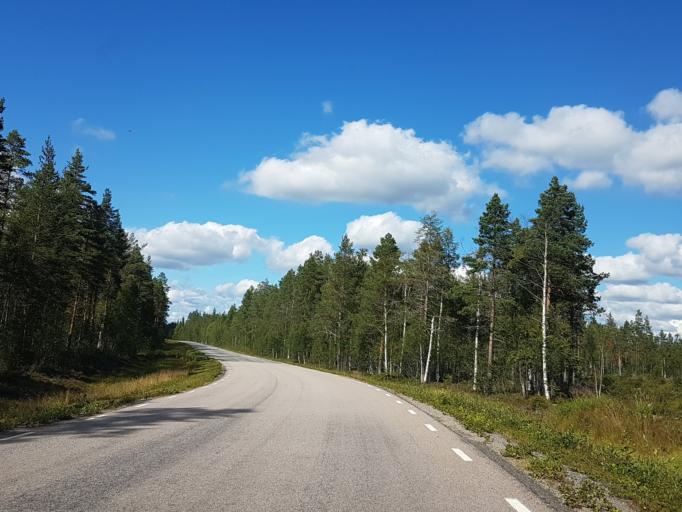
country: SE
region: Vaesterbotten
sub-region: Skelleftea Kommun
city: Burtraesk
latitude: 64.2408
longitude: 20.4838
